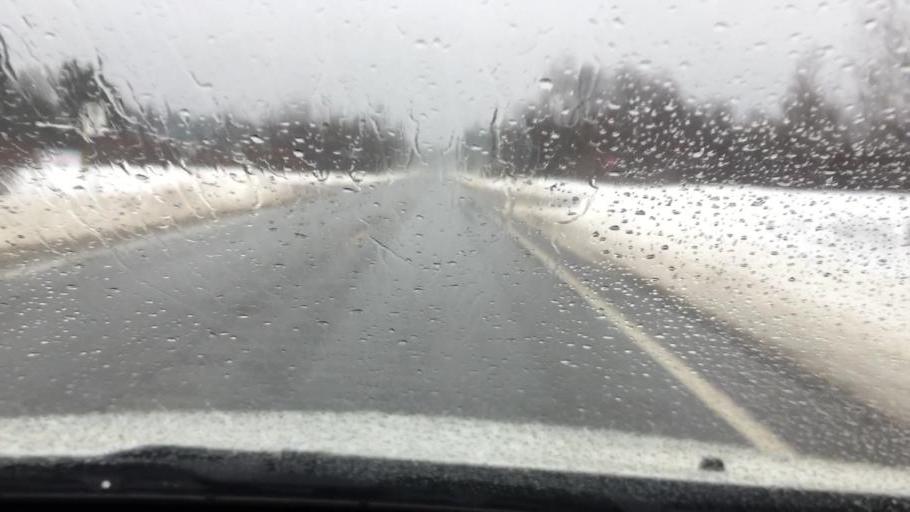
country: US
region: Michigan
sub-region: Charlevoix County
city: East Jordan
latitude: 45.0601
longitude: -85.0776
